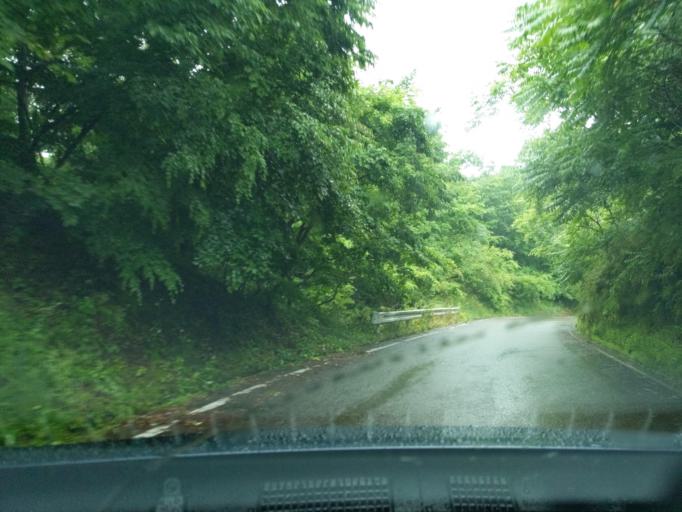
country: JP
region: Fukushima
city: Nihommatsu
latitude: 37.5763
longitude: 140.5524
